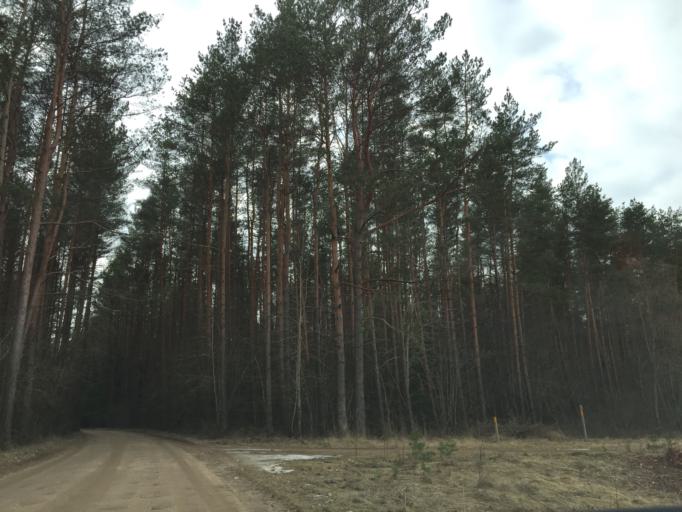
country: LV
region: Incukalns
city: Vangazi
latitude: 57.1034
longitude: 24.5467
